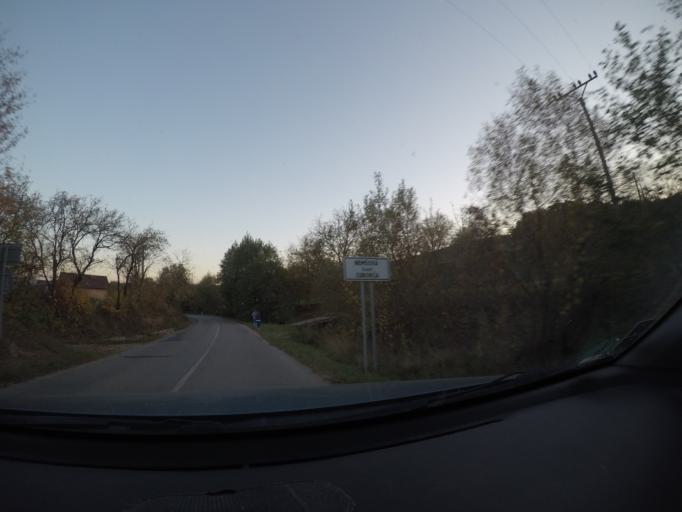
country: SK
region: Nitriansky
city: Nemsova
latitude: 48.9680
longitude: 18.0972
